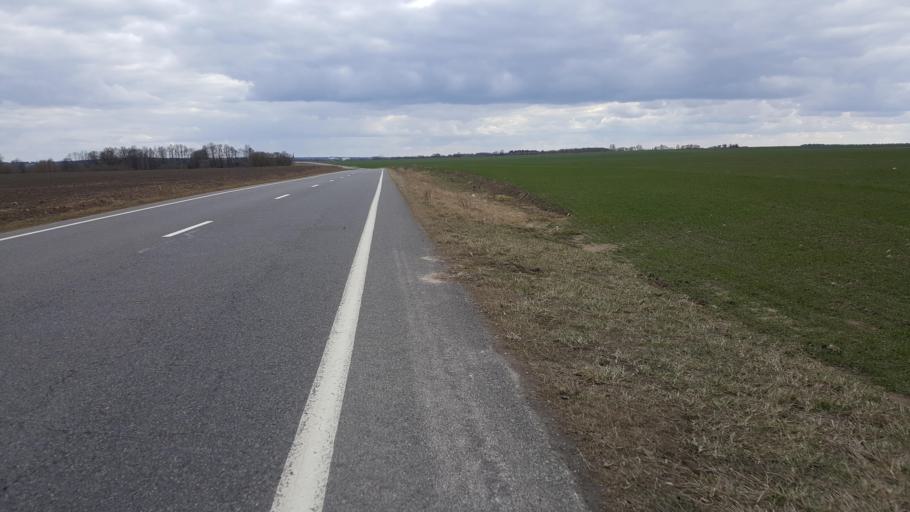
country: BY
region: Brest
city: Kamyanyets
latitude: 52.4433
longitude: 23.8321
